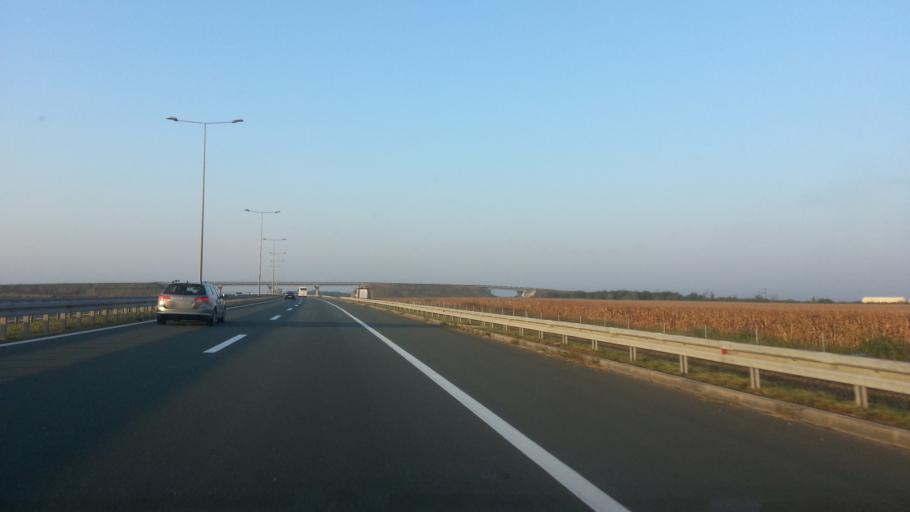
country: RS
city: Dobanovci
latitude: 44.8714
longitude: 20.2576
